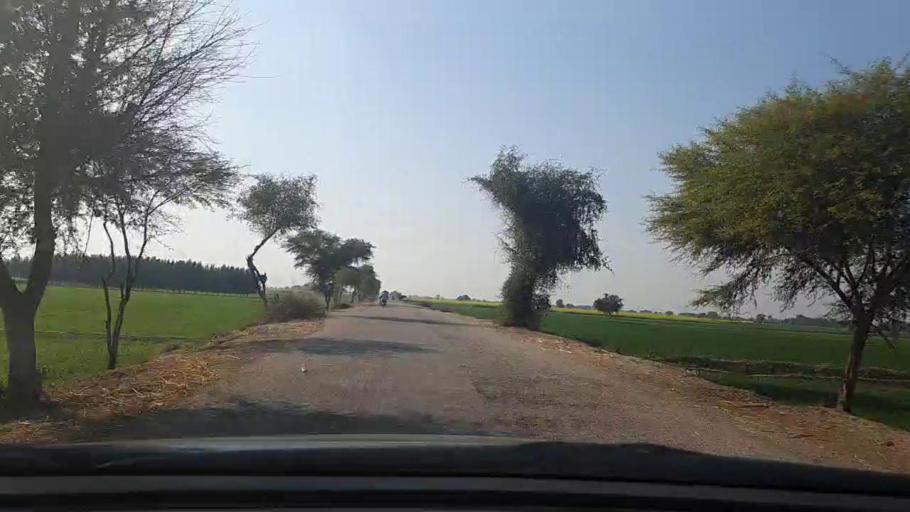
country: PK
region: Sindh
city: Daulatpur
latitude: 26.3200
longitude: 68.0409
